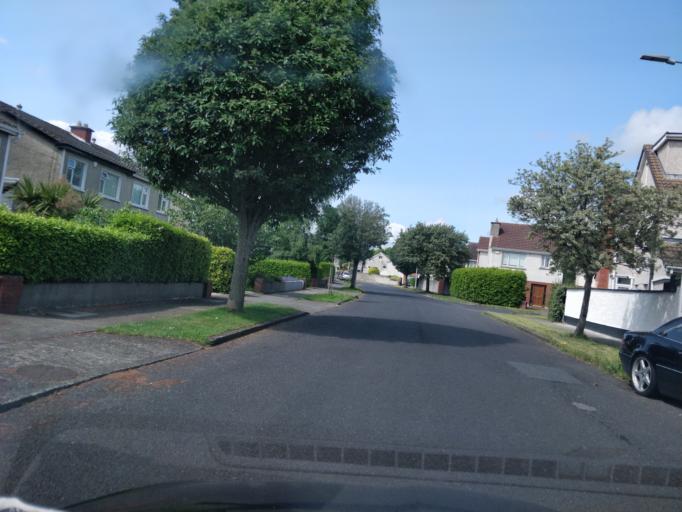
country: IE
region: Leinster
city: Dundrum
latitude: 53.2855
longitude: -6.2562
